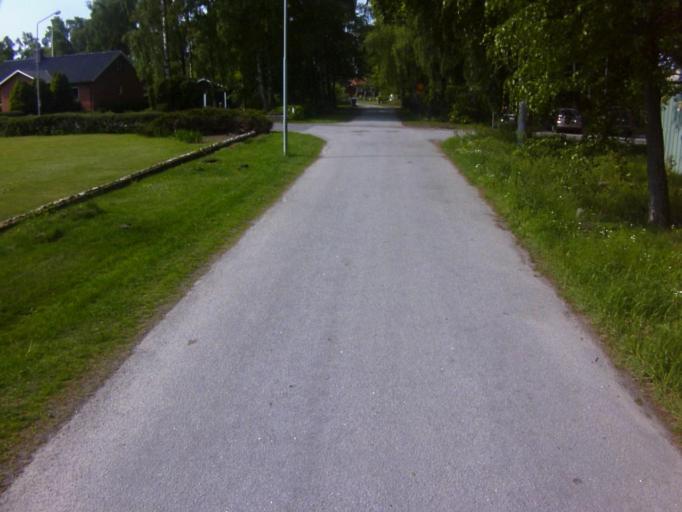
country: SE
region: Blekinge
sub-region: Solvesborgs Kommun
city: Soelvesborg
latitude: 56.0108
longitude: 14.7267
